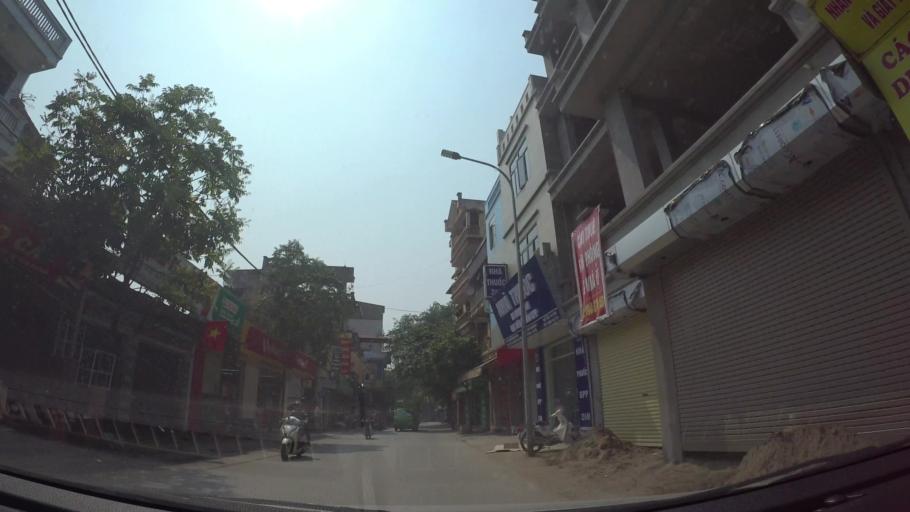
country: VN
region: Ha Noi
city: Ha Dong
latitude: 20.9952
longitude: 105.7584
